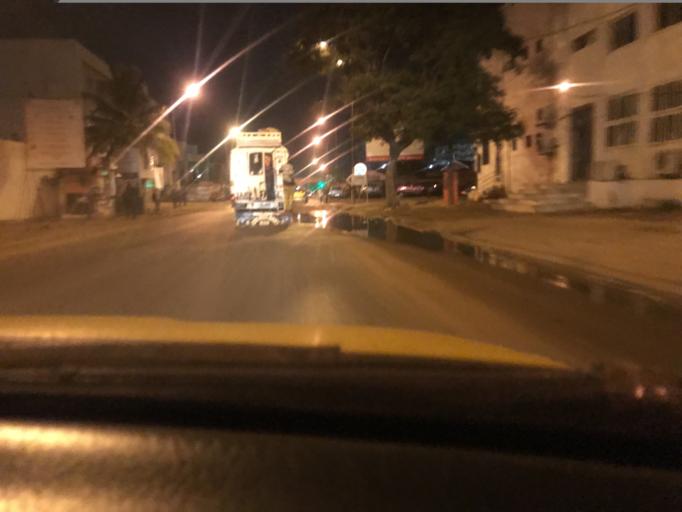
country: SN
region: Dakar
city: Dakar
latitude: 14.6809
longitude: -17.4416
